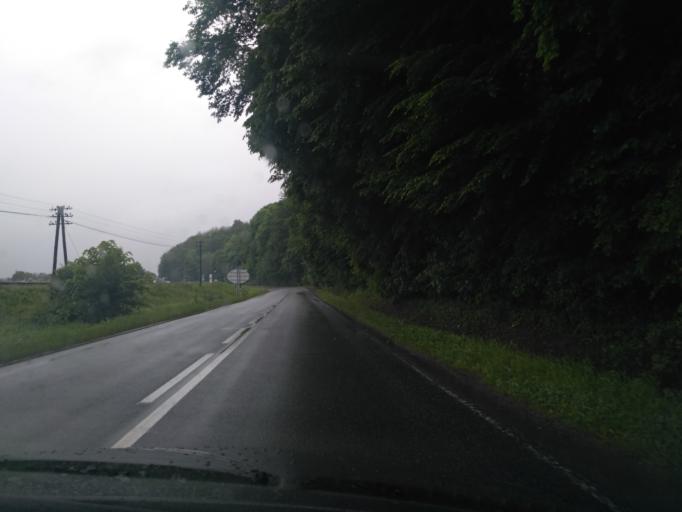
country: PL
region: Subcarpathian Voivodeship
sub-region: Powiat krosnienski
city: Leki
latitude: 49.8130
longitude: 21.6347
